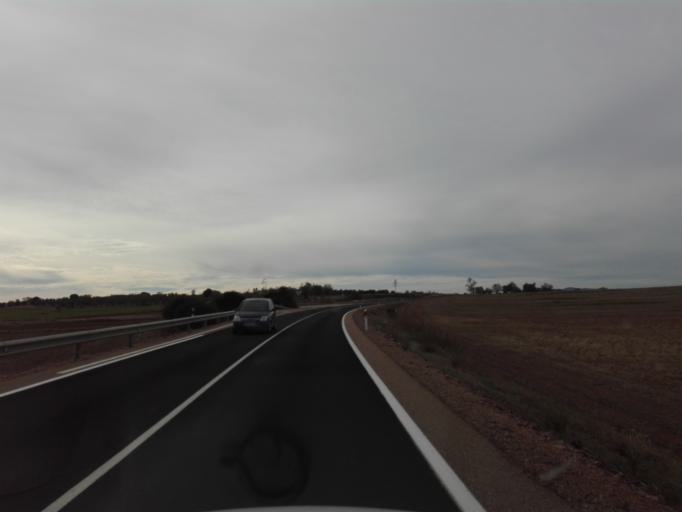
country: ES
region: Extremadura
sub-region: Provincia de Badajoz
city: Valencia de las Torres
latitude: 38.3244
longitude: -5.9633
